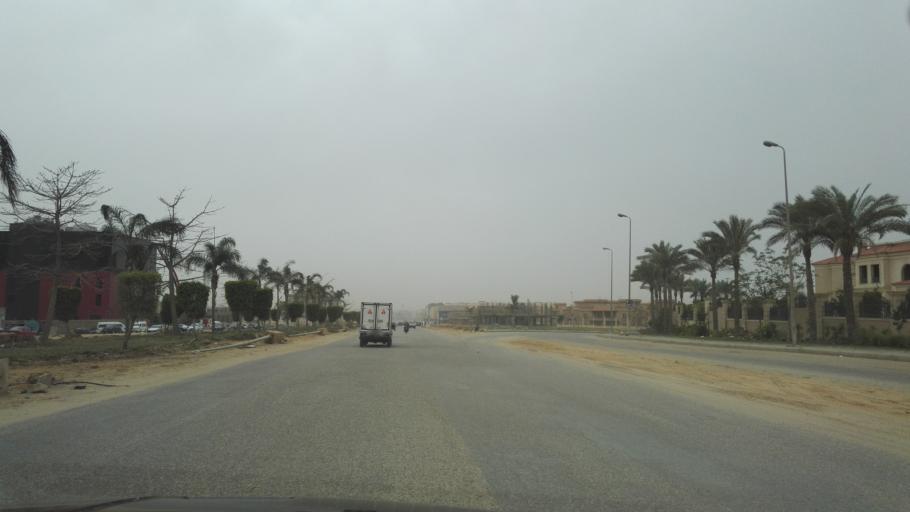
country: EG
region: Muhafazat al Qalyubiyah
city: Al Khankah
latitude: 30.0289
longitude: 31.4871
